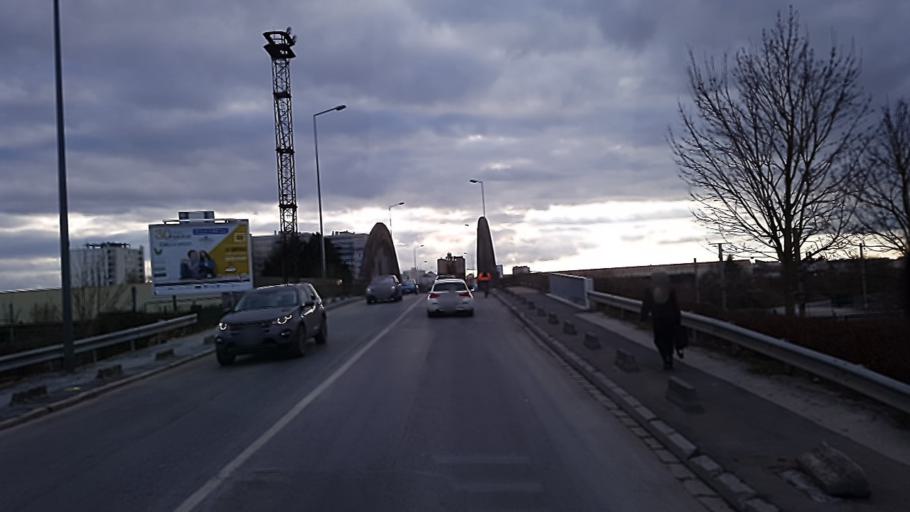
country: FR
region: Champagne-Ardenne
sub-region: Departement de la Marne
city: Betheny
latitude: 49.2672
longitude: 4.0656
